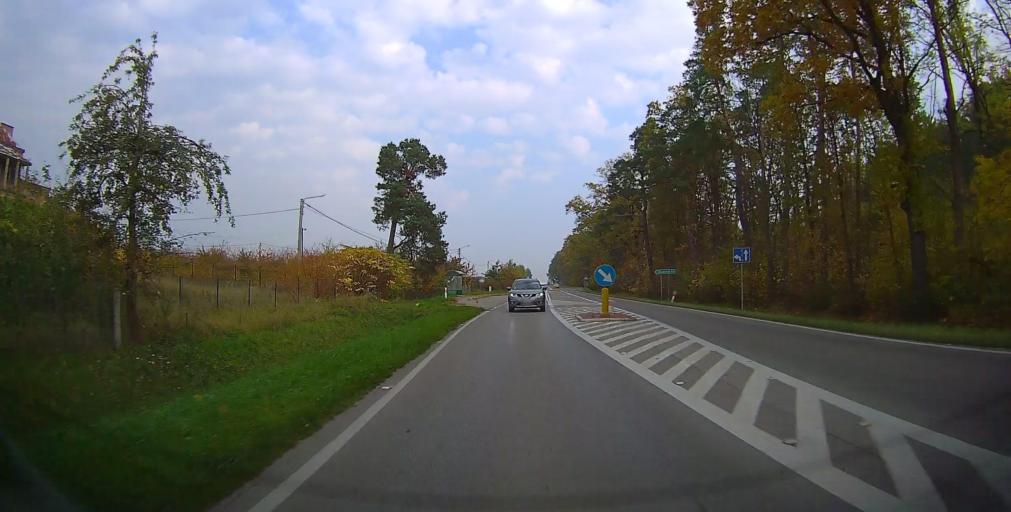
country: PL
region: Masovian Voivodeship
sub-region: Powiat grojecki
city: Belsk Duzy
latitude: 51.7945
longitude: 20.7854
